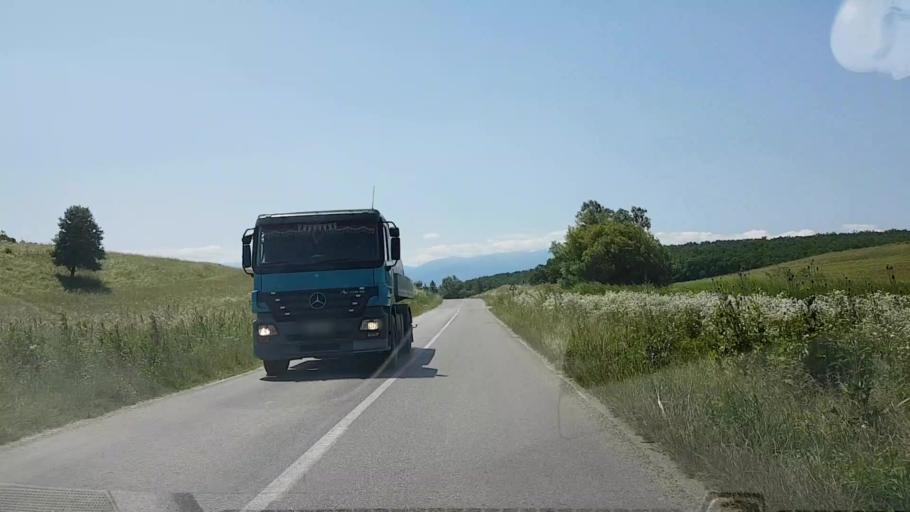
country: RO
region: Brasov
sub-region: Comuna Cincu
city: Cincu
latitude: 45.8906
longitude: 24.8117
